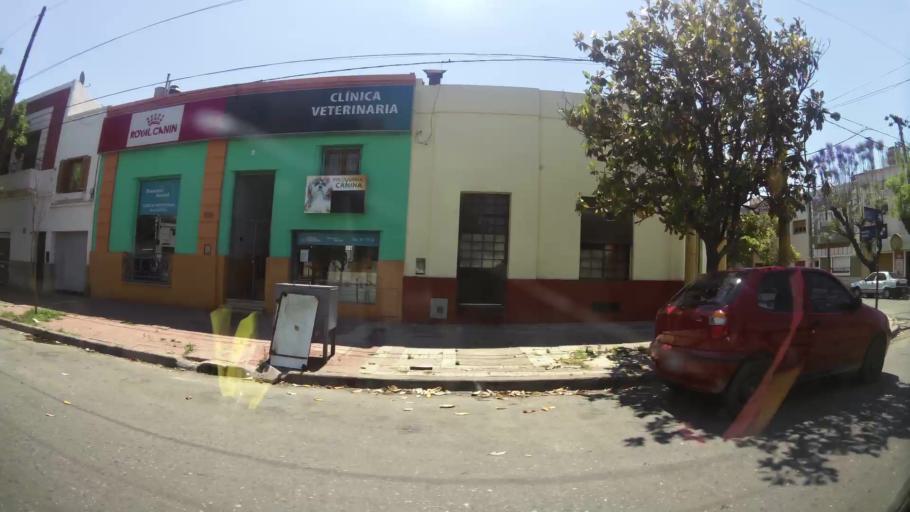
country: AR
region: Cordoba
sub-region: Departamento de Capital
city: Cordoba
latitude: -31.4006
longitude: -64.1864
